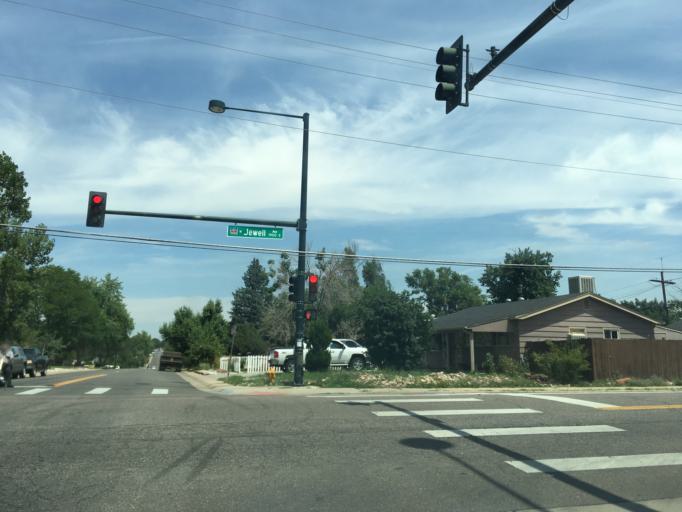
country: US
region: Colorado
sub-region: Arapahoe County
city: Sheridan
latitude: 39.6821
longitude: -105.0443
